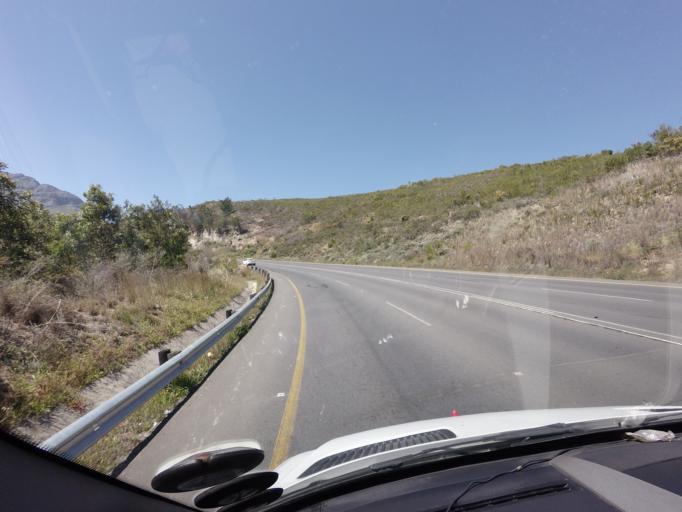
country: ZA
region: Western Cape
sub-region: Cape Winelands District Municipality
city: Stellenbosch
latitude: -33.9250
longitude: 18.9068
